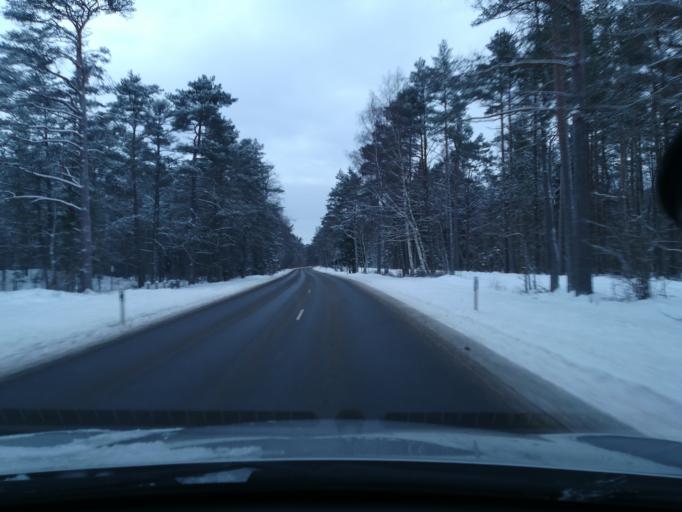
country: EE
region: Harju
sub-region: Paldiski linn
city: Paldiski
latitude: 59.3907
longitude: 24.2416
